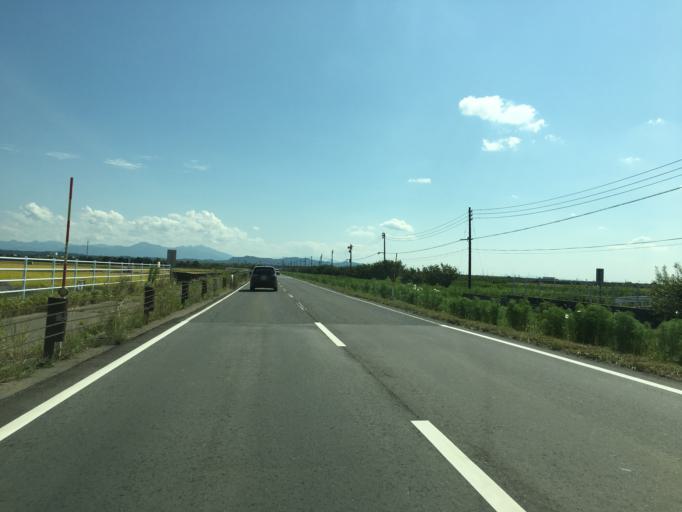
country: JP
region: Niigata
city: Niitsu-honcho
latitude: 37.8284
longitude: 139.0976
